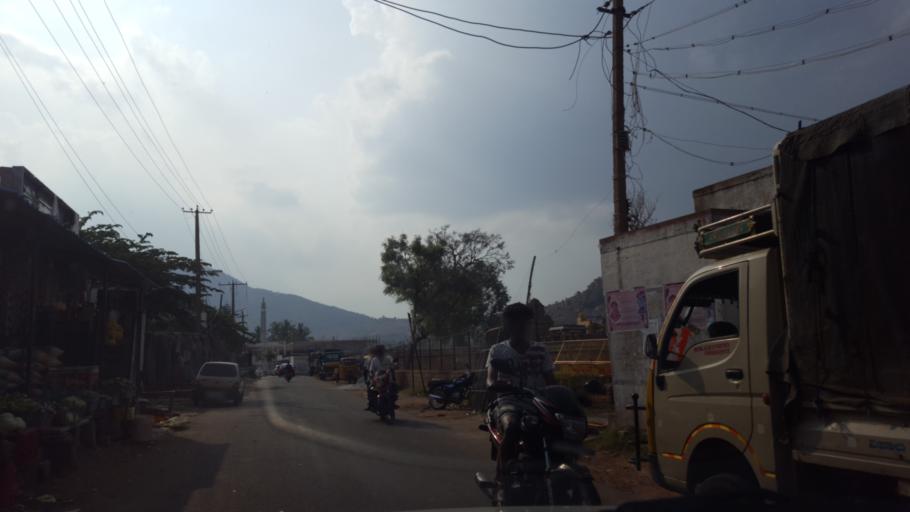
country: IN
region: Karnataka
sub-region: Chikkaballapur
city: Chik Ballapur
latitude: 13.3862
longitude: 77.6987
